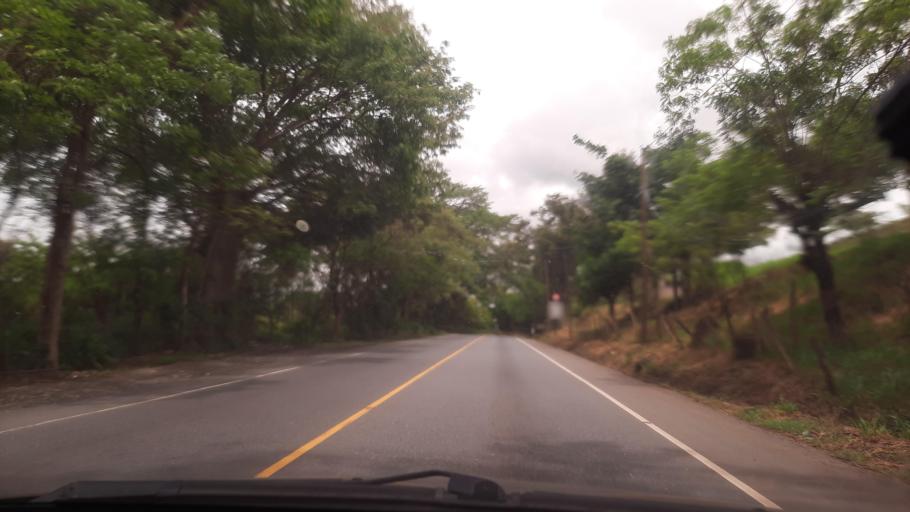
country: GT
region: Izabal
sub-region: Municipio de Los Amates
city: Los Amates
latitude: 15.2323
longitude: -89.1960
